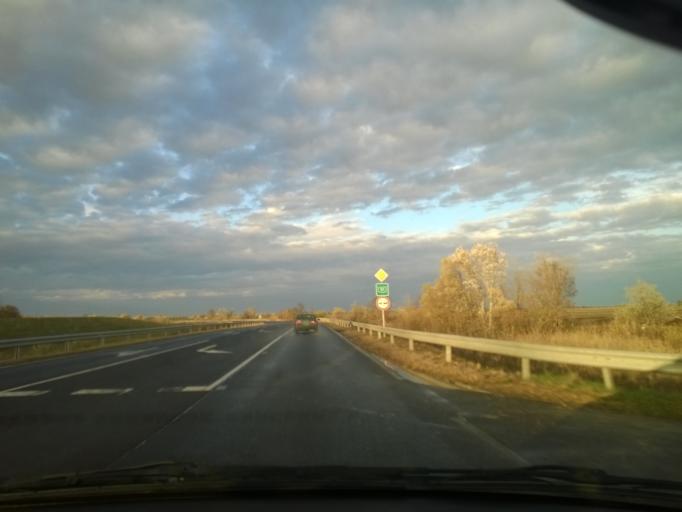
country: HU
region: Bacs-Kiskun
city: Dunapataj
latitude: 46.6572
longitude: 19.0092
